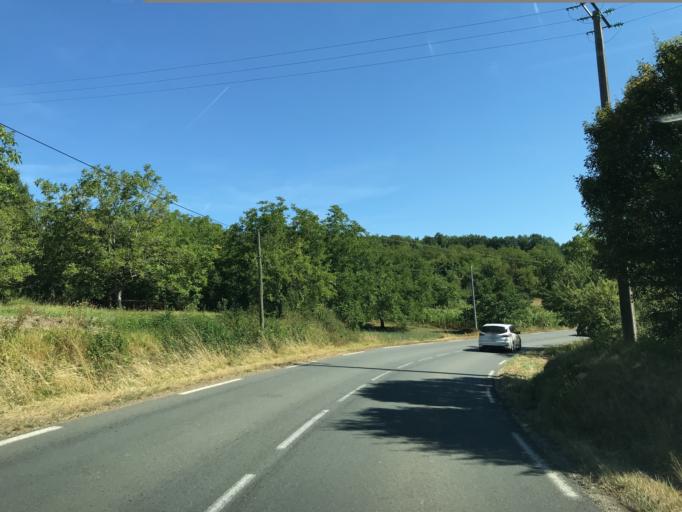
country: FR
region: Limousin
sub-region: Departement de la Correze
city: Larche
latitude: 45.0929
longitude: 1.3831
